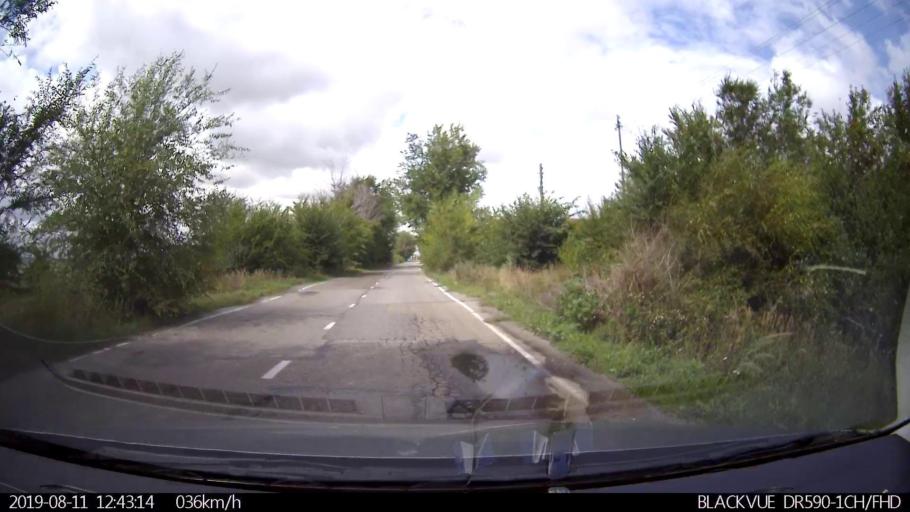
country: RU
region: Ulyanovsk
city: Ignatovka
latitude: 53.8500
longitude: 47.7442
